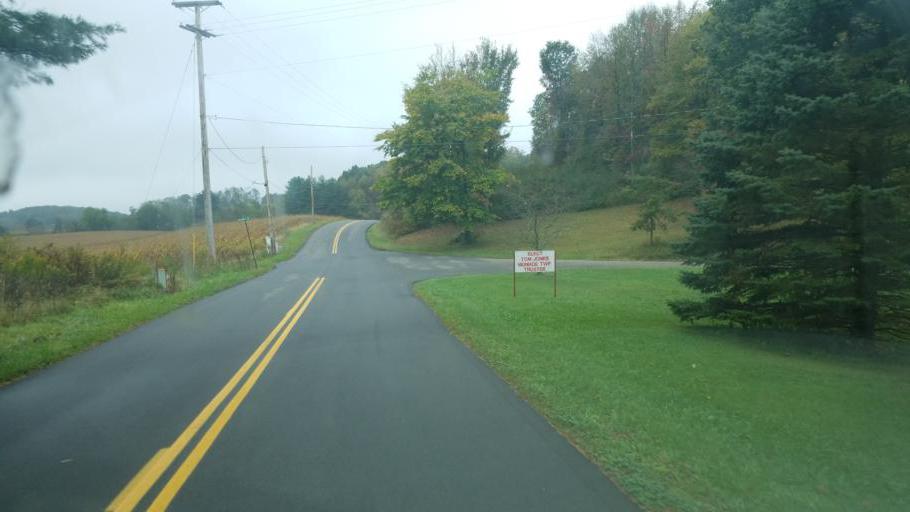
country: US
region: Ohio
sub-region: Carroll County
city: Carrollton
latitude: 40.5275
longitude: -81.1938
